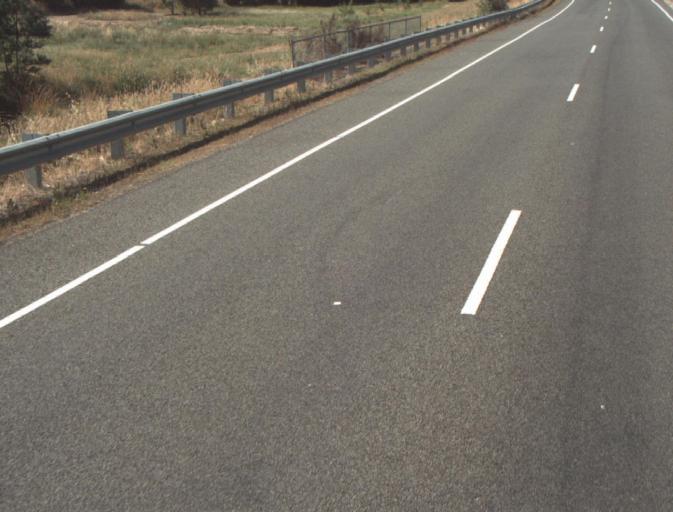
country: AU
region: Tasmania
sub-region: Launceston
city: Newstead
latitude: -41.4291
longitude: 147.1869
